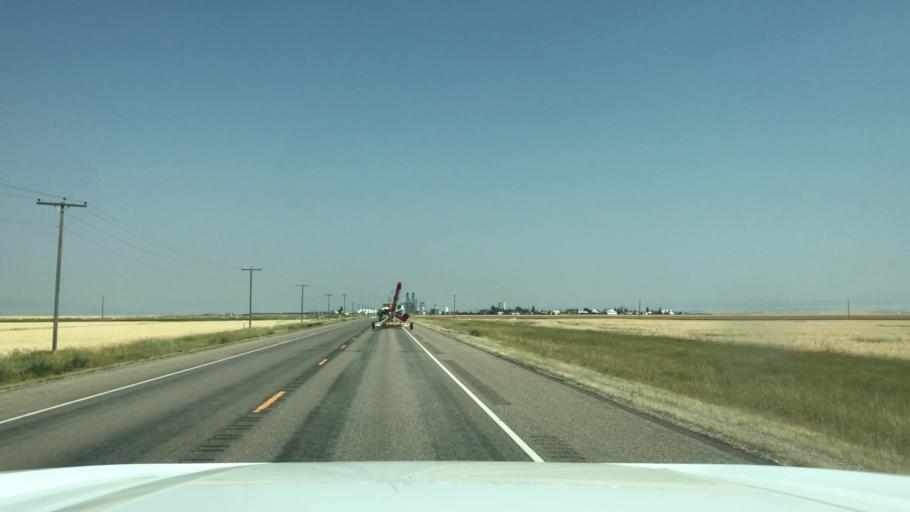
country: US
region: Montana
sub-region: Judith Basin County
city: Stanford
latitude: 47.0552
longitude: -109.9312
